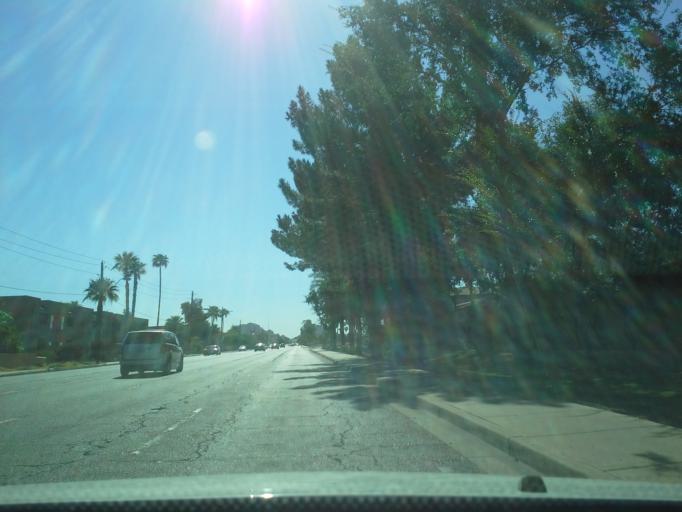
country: US
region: Arizona
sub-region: Maricopa County
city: Phoenix
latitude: 33.4657
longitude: -112.0016
